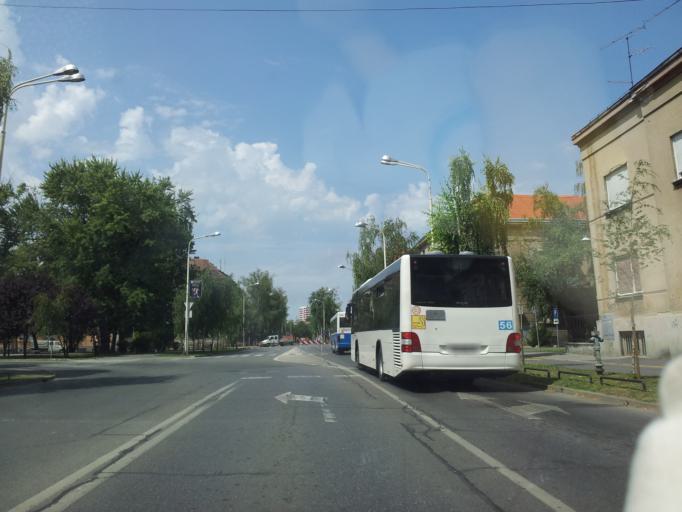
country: HR
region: Osjecko-Baranjska
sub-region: Grad Osijek
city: Osijek
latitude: 45.5568
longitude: 18.6874
